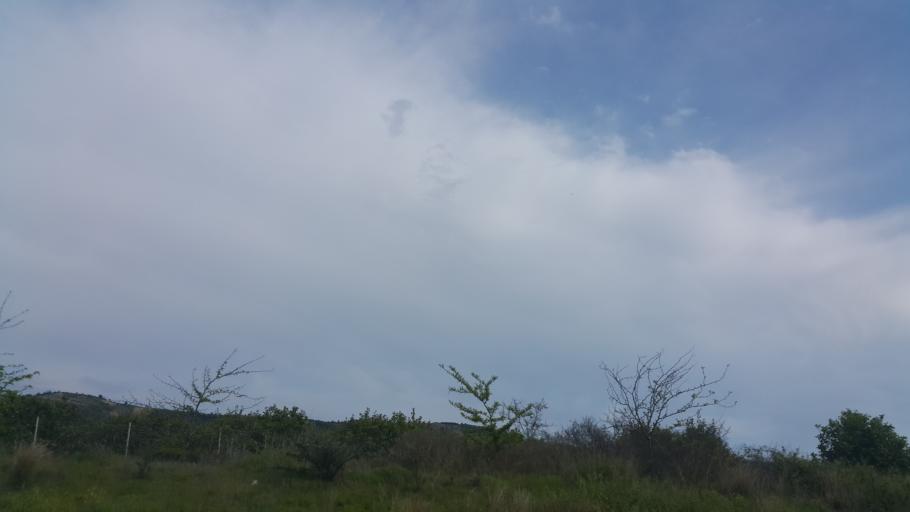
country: TR
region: Mersin
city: Kazanli
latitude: 36.9468
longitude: 34.7308
